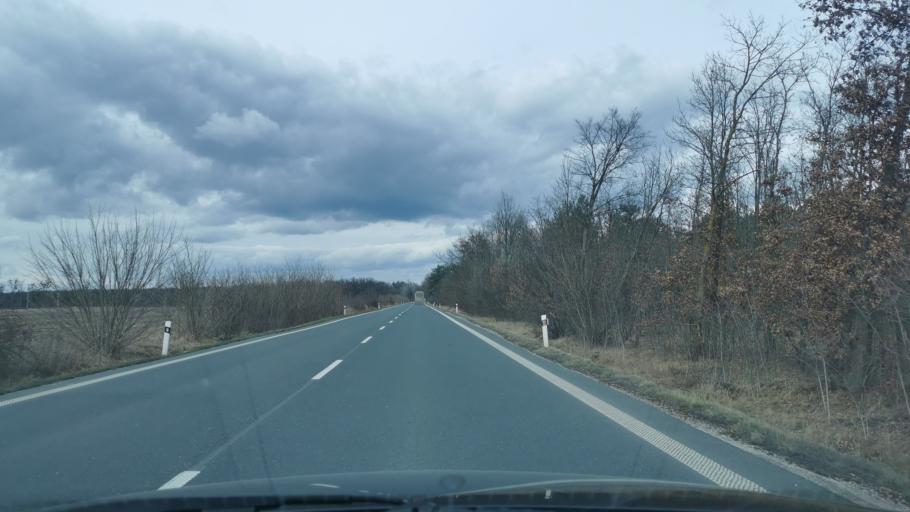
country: CZ
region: South Moravian
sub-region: Okres Breclav
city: Lanzhot
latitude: 48.6943
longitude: 17.0374
